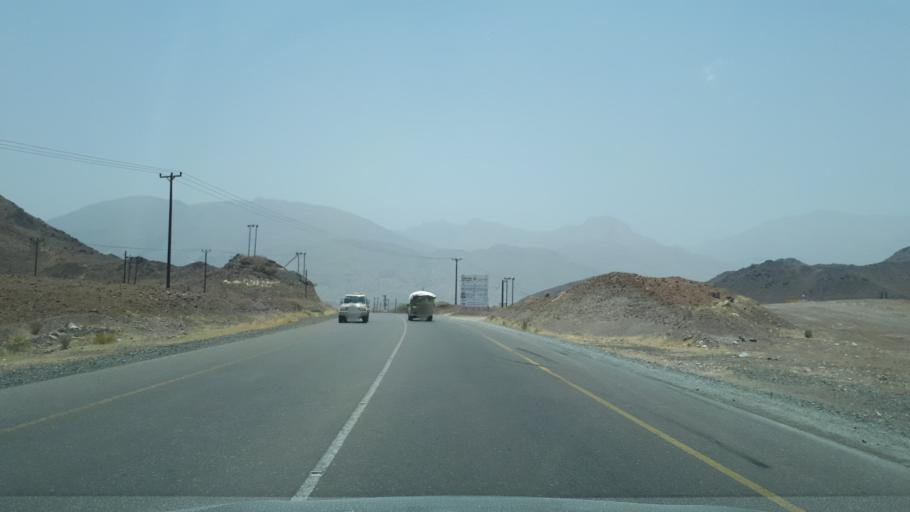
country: OM
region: Al Batinah
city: Rustaq
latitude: 23.4237
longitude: 57.2611
